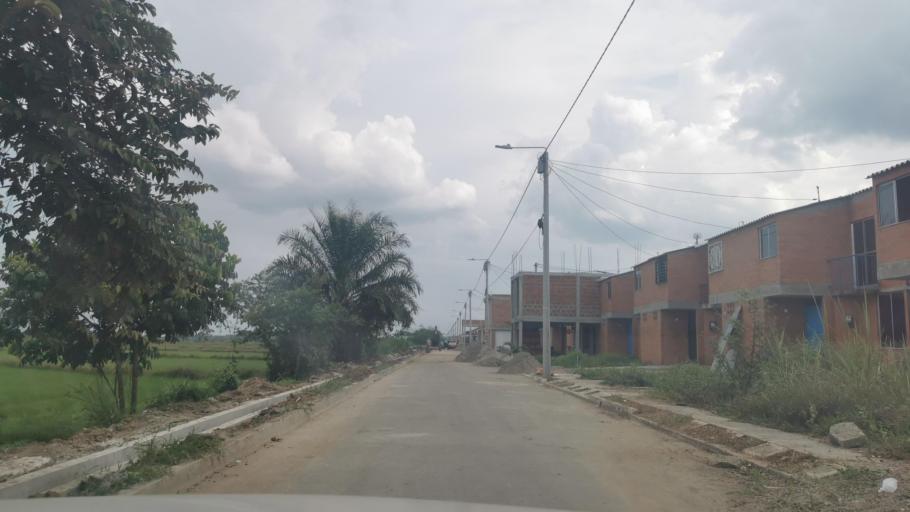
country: CO
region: Valle del Cauca
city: Jamundi
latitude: 3.2360
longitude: -76.5244
